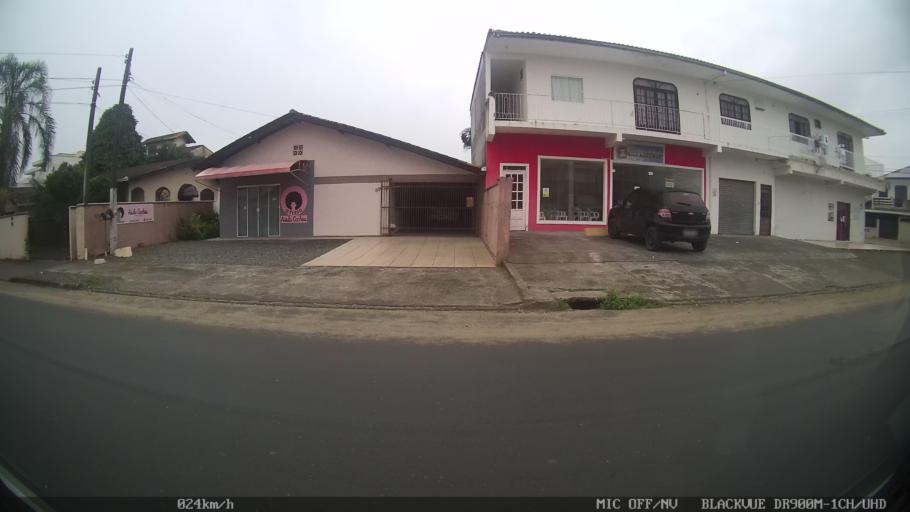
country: BR
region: Santa Catarina
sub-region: Joinville
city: Joinville
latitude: -26.2682
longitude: -48.8007
